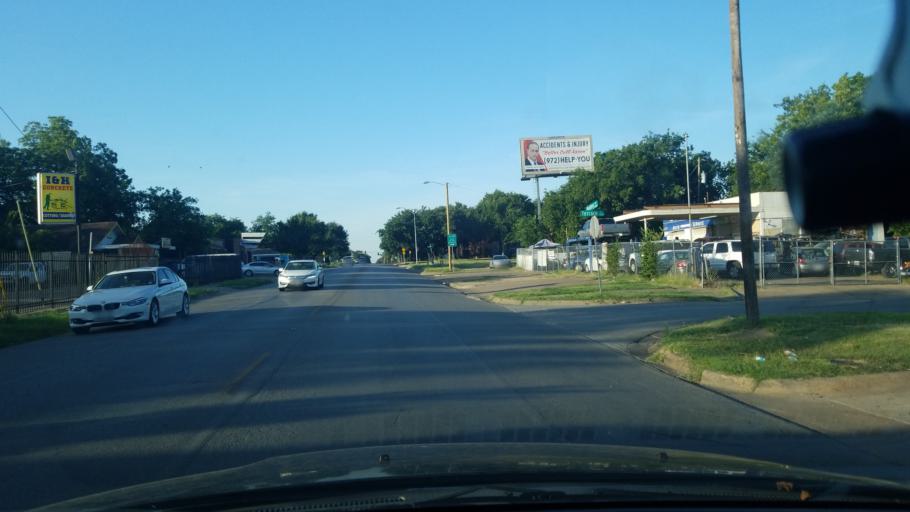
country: US
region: Texas
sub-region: Dallas County
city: Cockrell Hill
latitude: 32.7161
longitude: -96.8229
